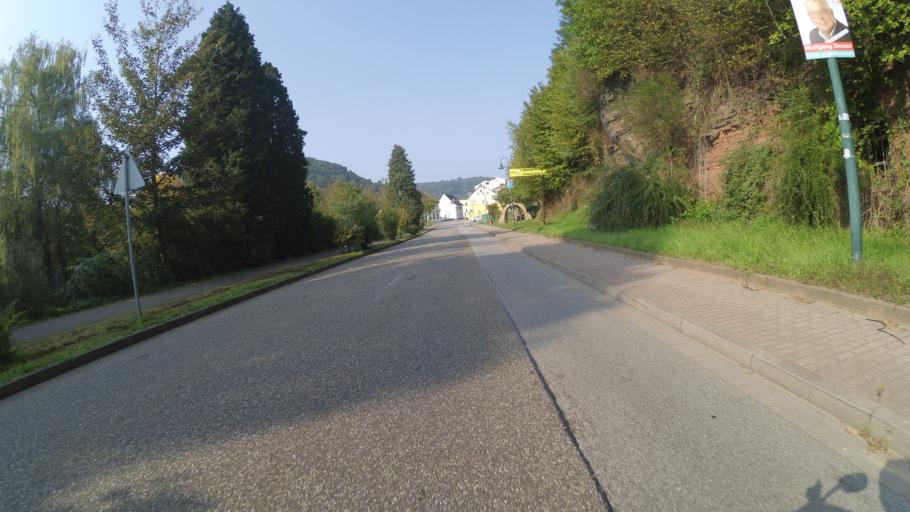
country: DE
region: Rheinland-Pfalz
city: Rodalben
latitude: 49.2384
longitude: 7.6406
